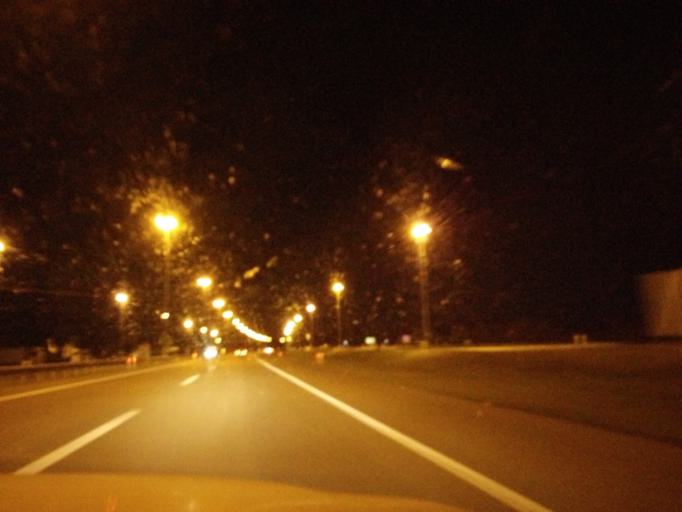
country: HR
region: Brodsko-Posavska
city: Garcin
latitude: 45.1478
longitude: 18.2774
